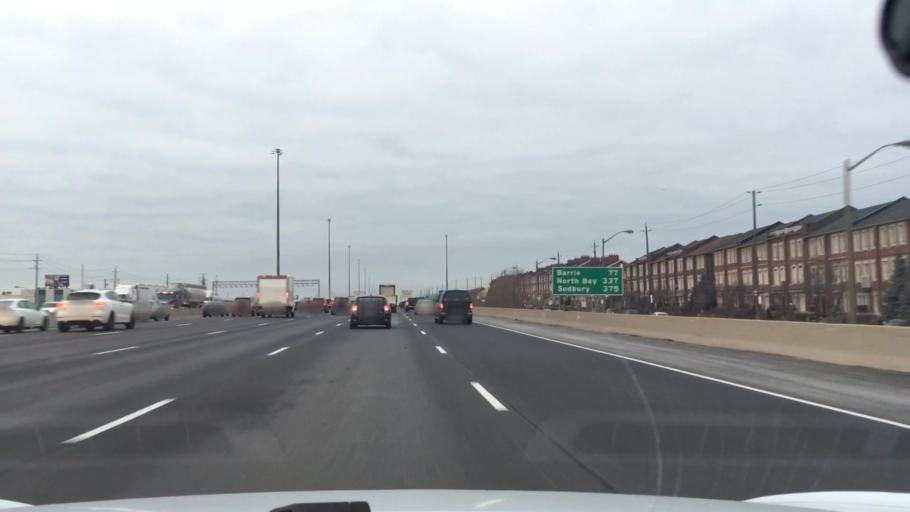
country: CA
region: Ontario
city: Etobicoke
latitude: 43.7262
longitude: -79.5237
